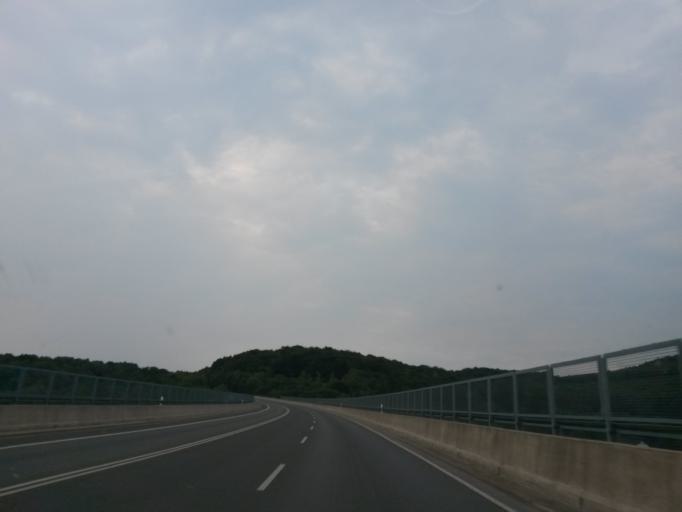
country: DE
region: North Rhine-Westphalia
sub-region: Regierungsbezirk Arnsberg
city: Hagen
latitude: 51.3408
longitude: 7.5085
